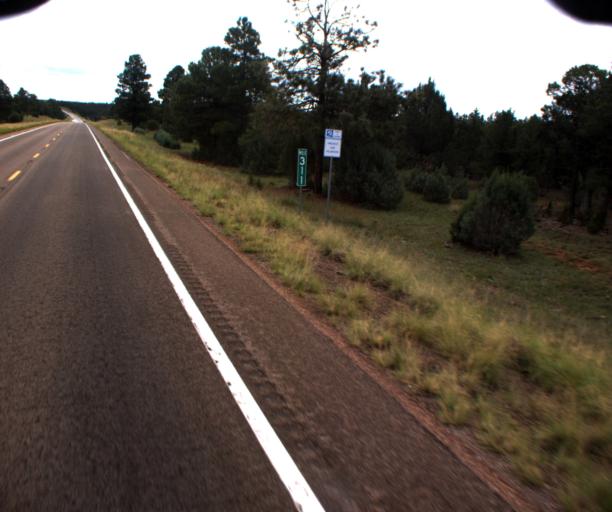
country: US
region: Arizona
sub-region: Navajo County
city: Heber-Overgaard
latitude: 34.3882
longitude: -110.5022
